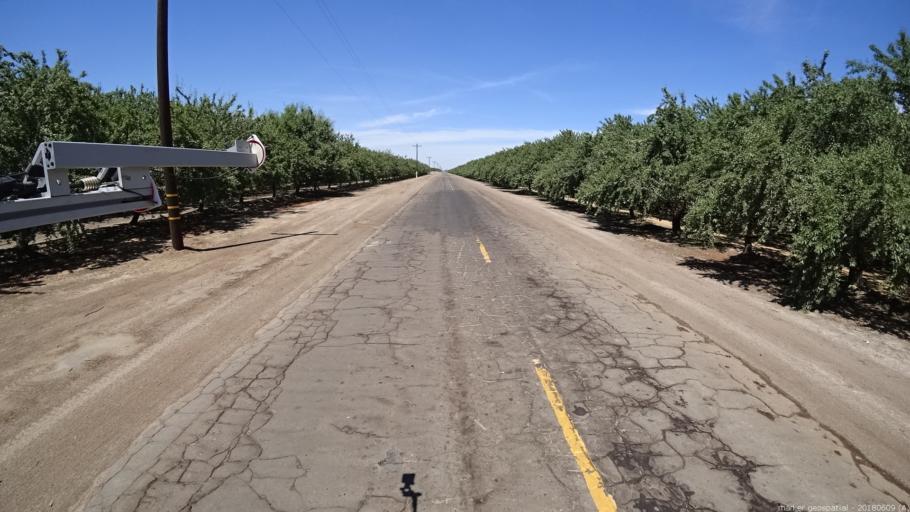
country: US
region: California
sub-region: Madera County
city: Fairmead
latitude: 36.9383
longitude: -120.2259
